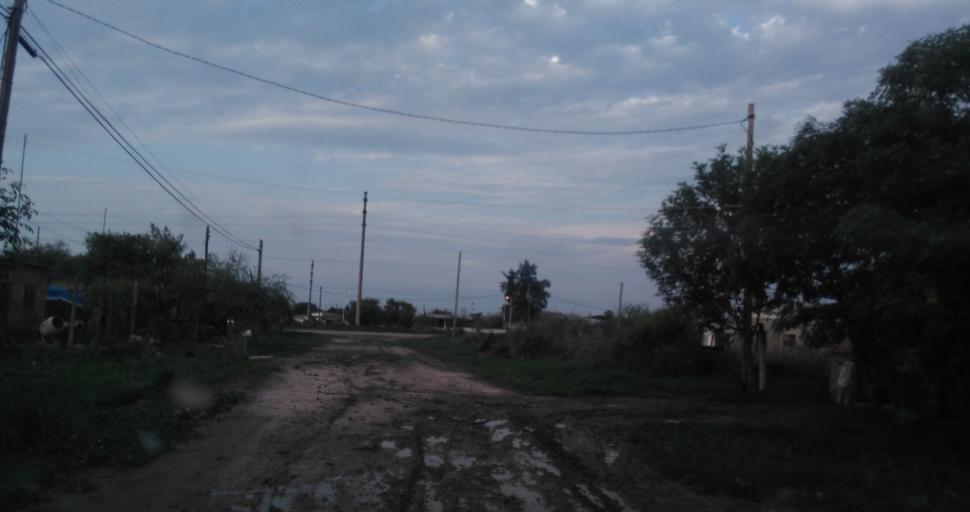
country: AR
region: Chaco
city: Resistencia
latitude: -27.4788
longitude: -59.0013
